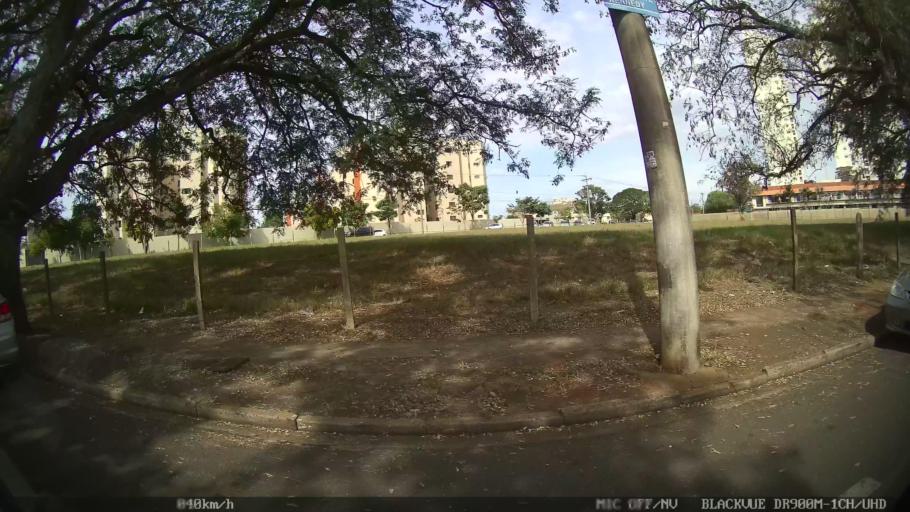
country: BR
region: Sao Paulo
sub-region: Piracicaba
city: Piracicaba
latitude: -22.7163
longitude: -47.6593
